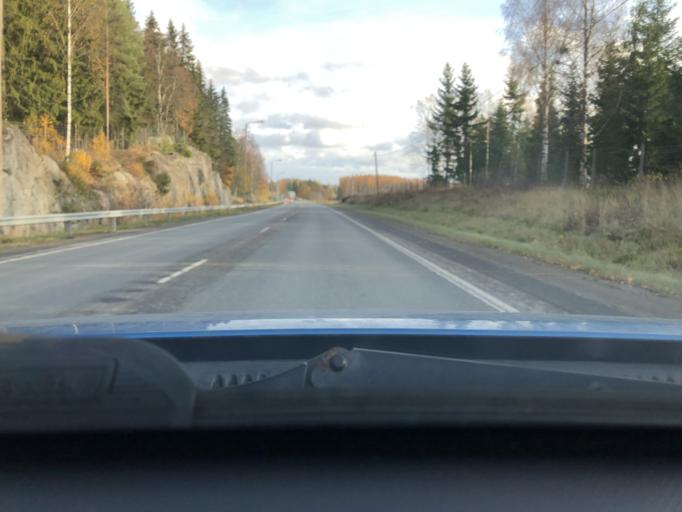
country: FI
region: Pirkanmaa
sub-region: Tampere
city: Kangasala
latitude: 61.4668
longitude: 24.0010
